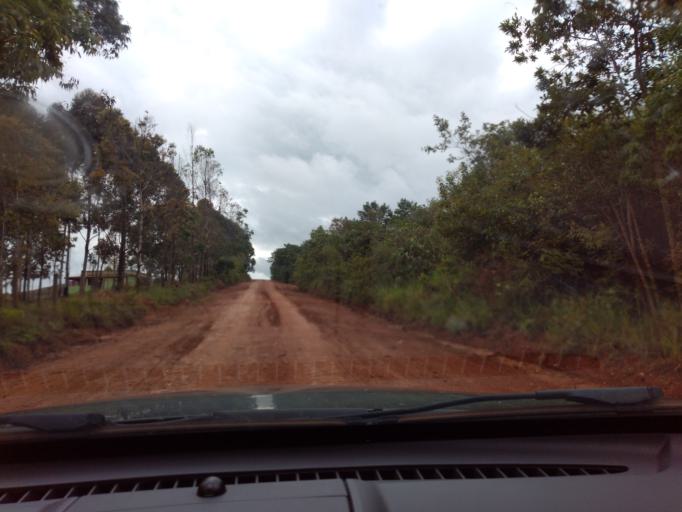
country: BR
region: Minas Gerais
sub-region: Lavras
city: Lavras
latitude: -21.5103
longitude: -44.9266
